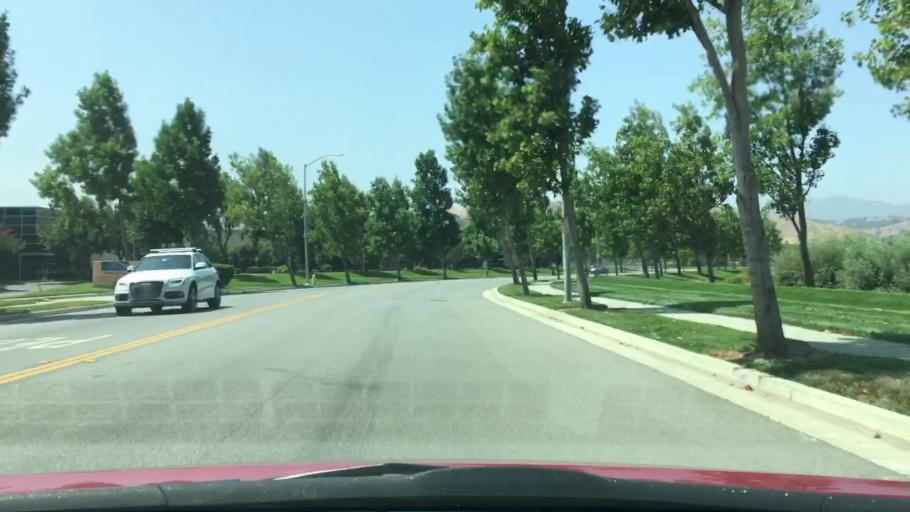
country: US
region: California
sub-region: Santa Clara County
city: Morgan Hill
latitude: 37.1534
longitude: -121.6602
